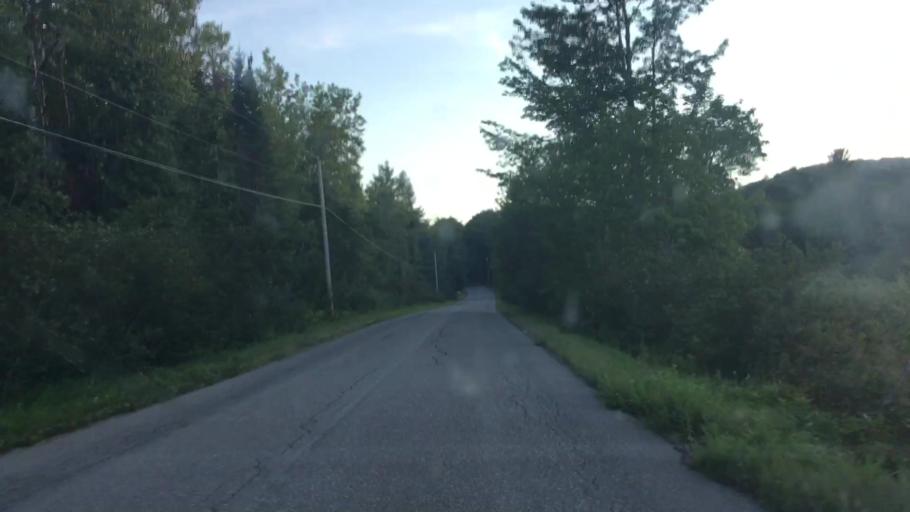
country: US
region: Maine
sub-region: Waldo County
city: Frankfort
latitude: 44.6610
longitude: -68.9312
